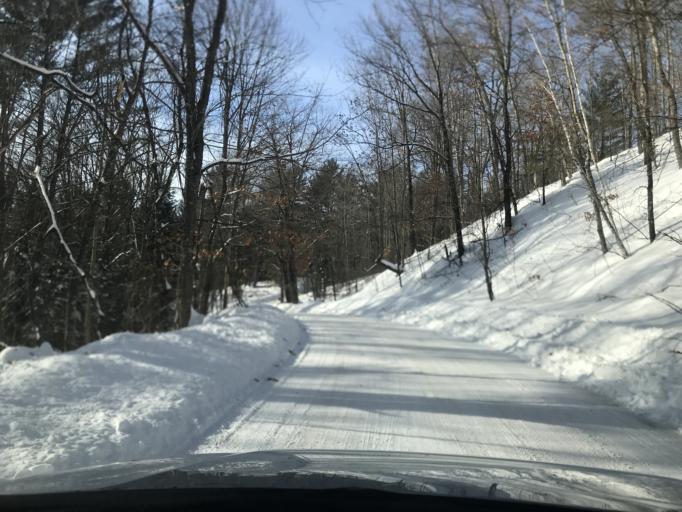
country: US
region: Wisconsin
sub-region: Menominee County
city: Legend Lake
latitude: 45.3439
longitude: -88.4561
